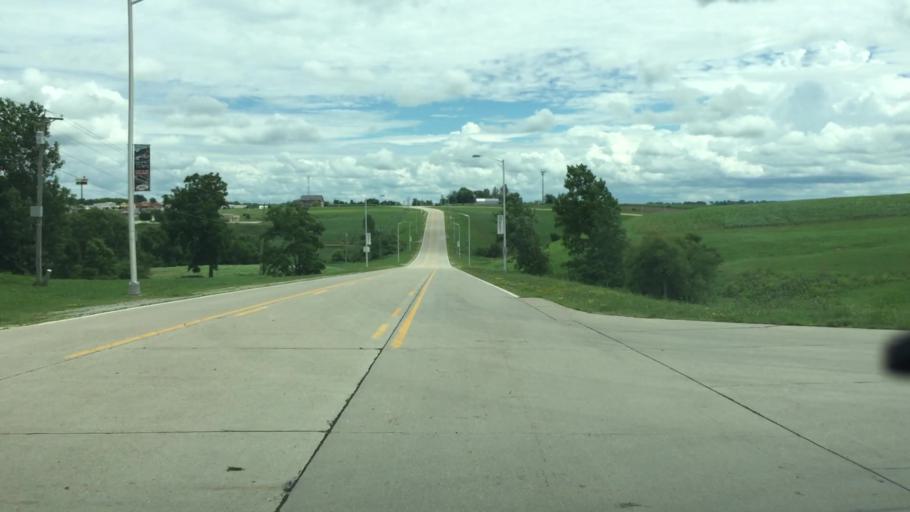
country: US
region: Iowa
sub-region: Jasper County
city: Newton
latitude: 41.6777
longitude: -93.0098
